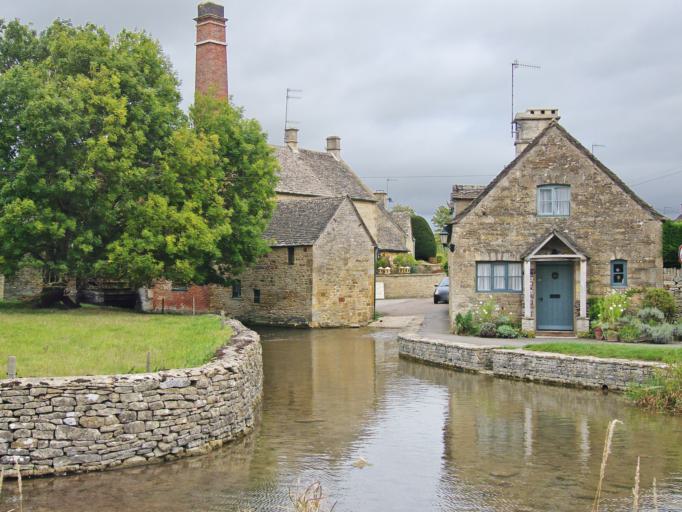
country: GB
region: England
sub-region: Gloucestershire
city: Bourton on the Water
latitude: 51.9013
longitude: -1.7639
